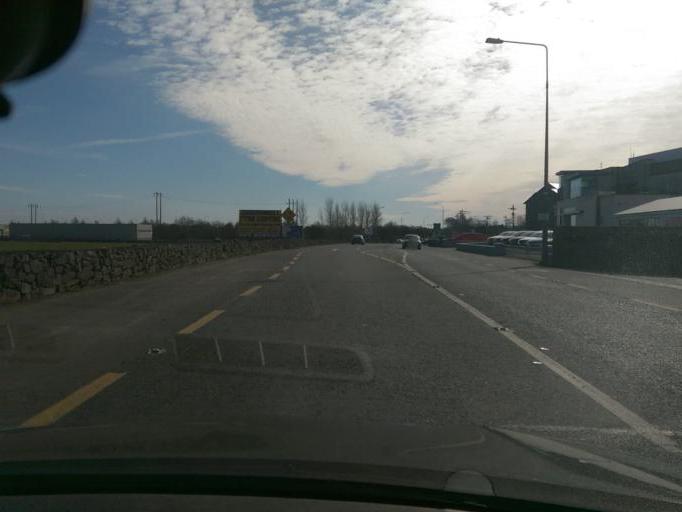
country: IE
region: Connaught
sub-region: County Galway
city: Oranmore
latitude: 53.2797
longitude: -8.9259
